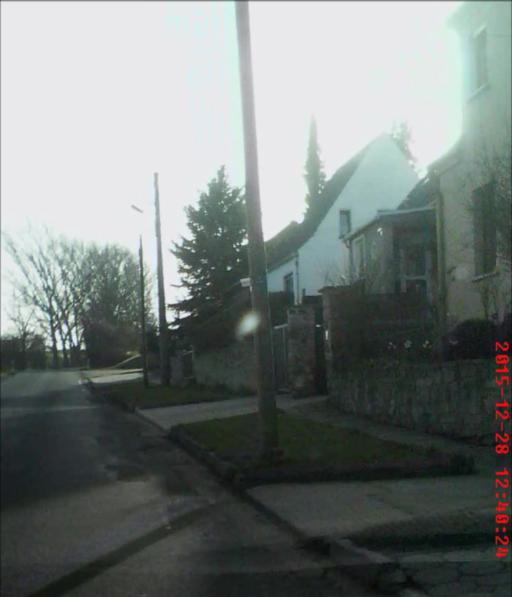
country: DE
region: Thuringia
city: Ossmanstedt
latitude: 51.0103
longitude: 11.4248
